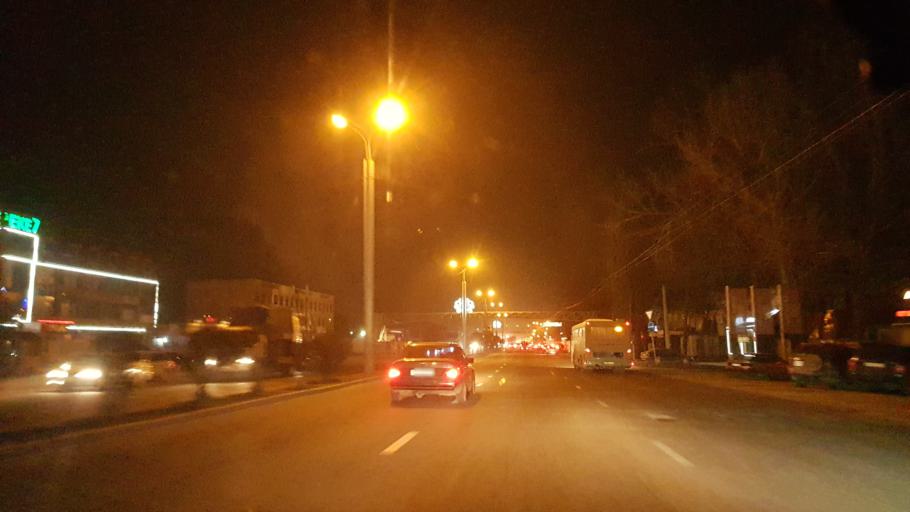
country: KZ
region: Almaty Qalasy
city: Almaty
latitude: 43.2613
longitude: 76.8554
